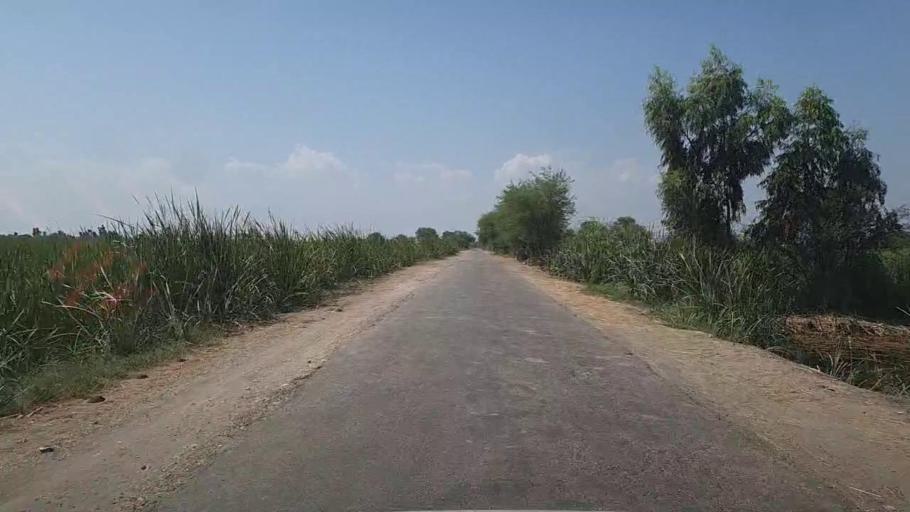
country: PK
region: Sindh
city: Khairpur
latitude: 28.0728
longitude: 69.6405
